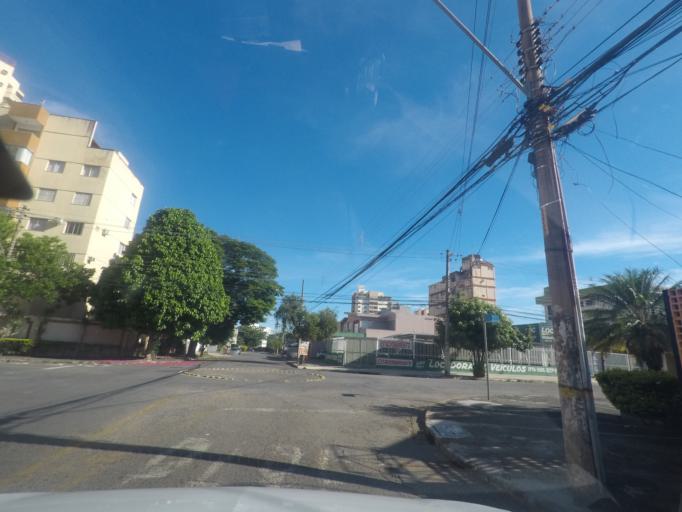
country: BR
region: Goias
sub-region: Goiania
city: Goiania
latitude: -16.6750
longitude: -49.2702
